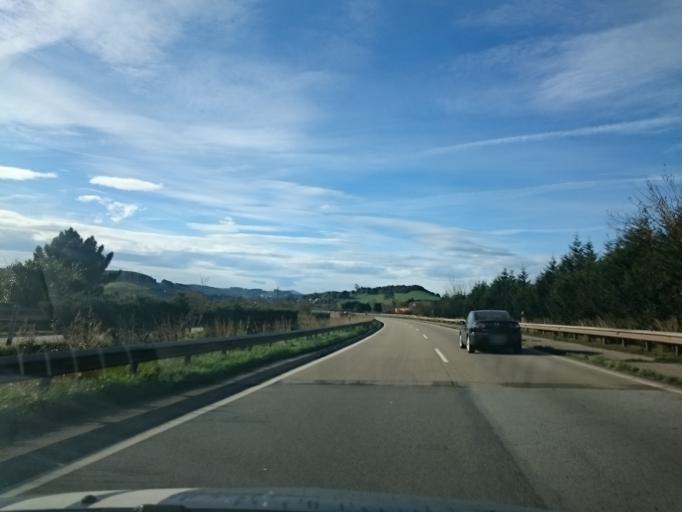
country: ES
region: Asturias
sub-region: Province of Asturias
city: Natahoyo
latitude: 43.5038
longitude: -5.7486
